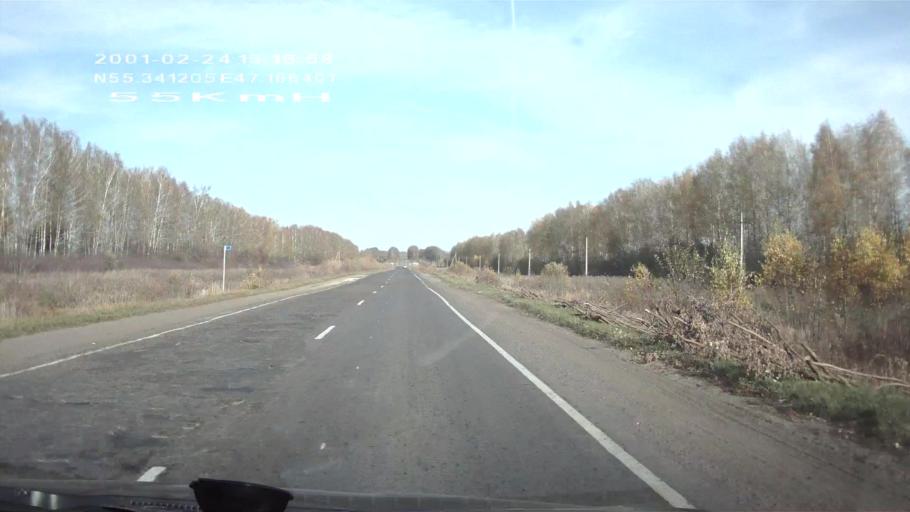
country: RU
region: Chuvashia
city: Ibresi
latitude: 55.3412
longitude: 47.1664
